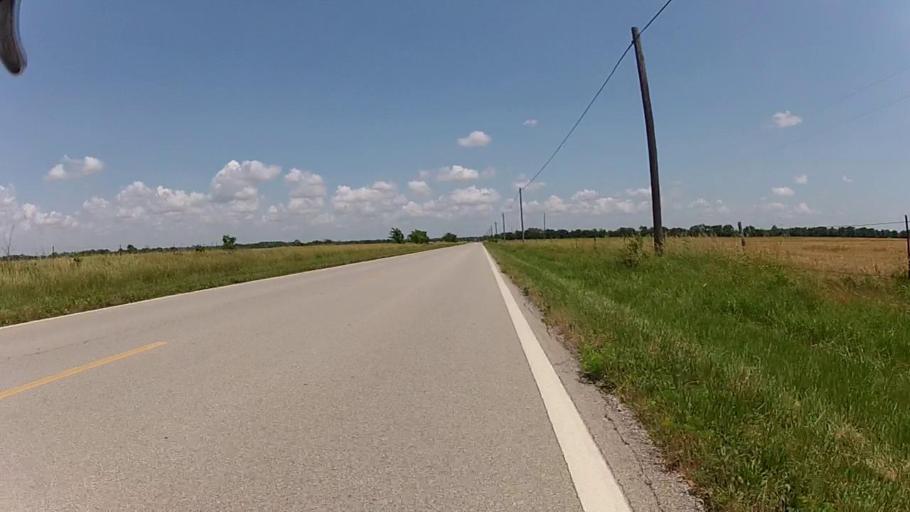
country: US
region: Kansas
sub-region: Labette County
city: Altamont
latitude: 37.1924
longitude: -95.4255
